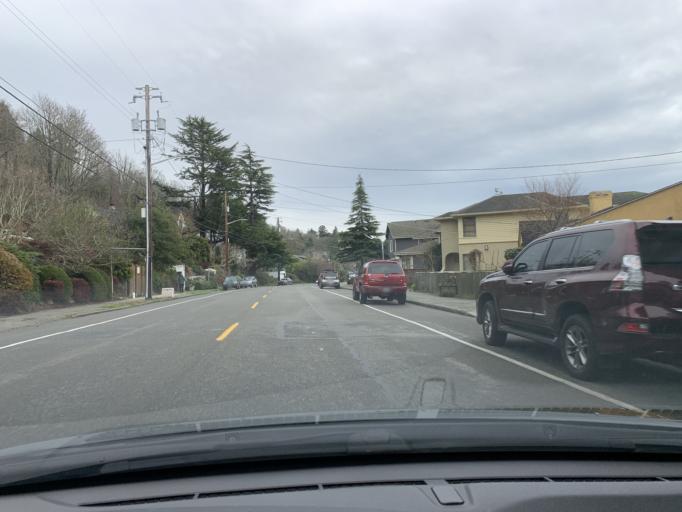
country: US
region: Washington
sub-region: King County
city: White Center
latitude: 47.5560
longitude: -122.4000
